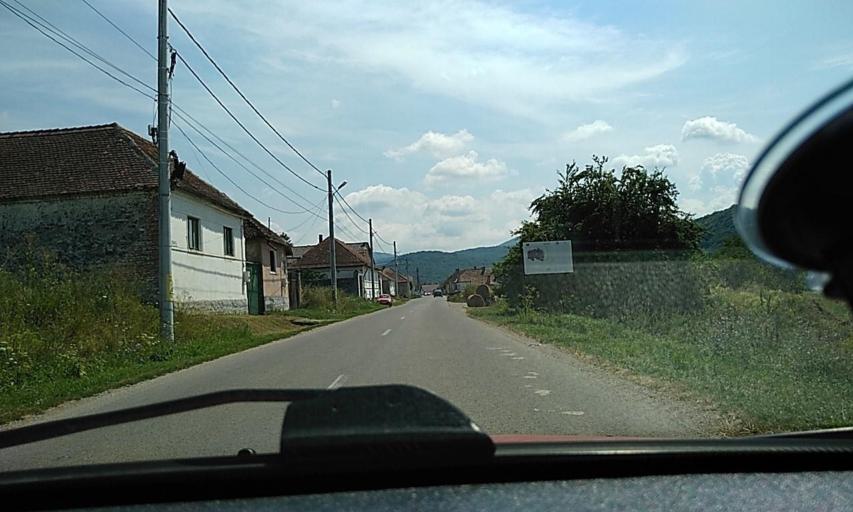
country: RO
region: Brasov
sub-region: Comuna Hoghiz
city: Hoghiz
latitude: 46.0267
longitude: 25.3957
